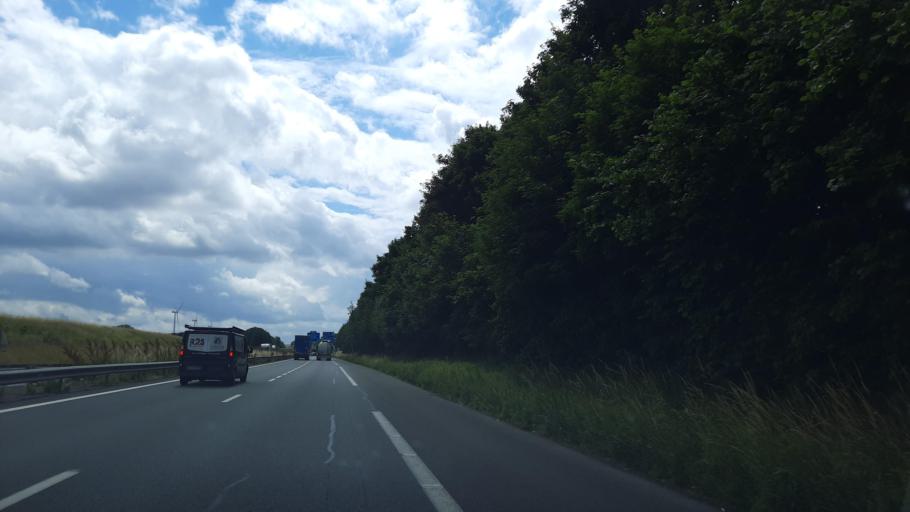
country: FR
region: Nord-Pas-de-Calais
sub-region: Departement du Pas-de-Calais
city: Bourlon
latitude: 50.1489
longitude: 3.1187
